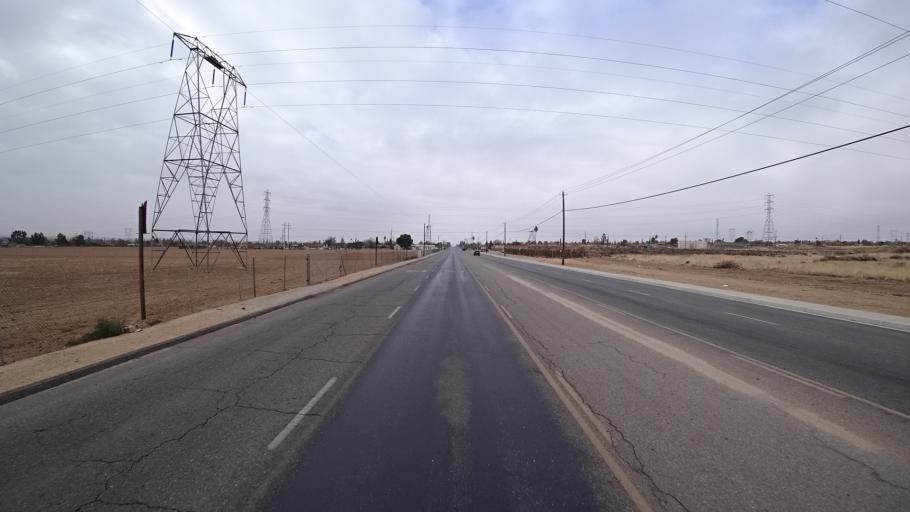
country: US
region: California
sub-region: Kern County
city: Bakersfield
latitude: 35.3761
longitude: -118.9200
